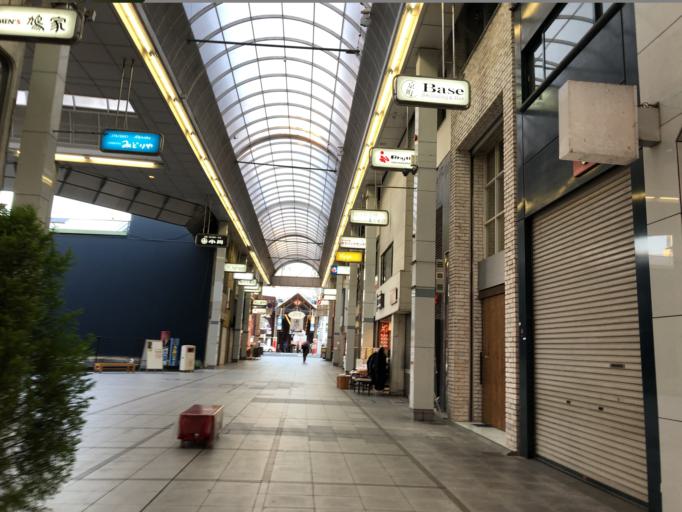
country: JP
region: Kochi
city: Kochi-shi
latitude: 33.5605
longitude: 133.5415
